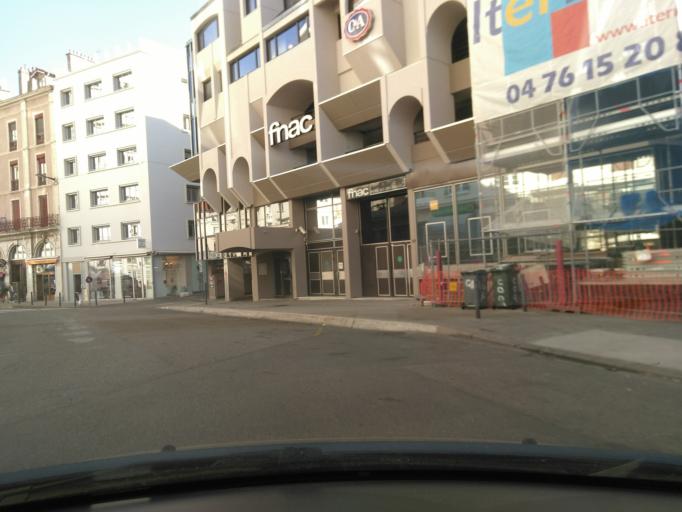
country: FR
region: Rhone-Alpes
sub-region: Departement de l'Isere
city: Saint-Martin-le-Vinoux
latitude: 45.1906
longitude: 5.7250
